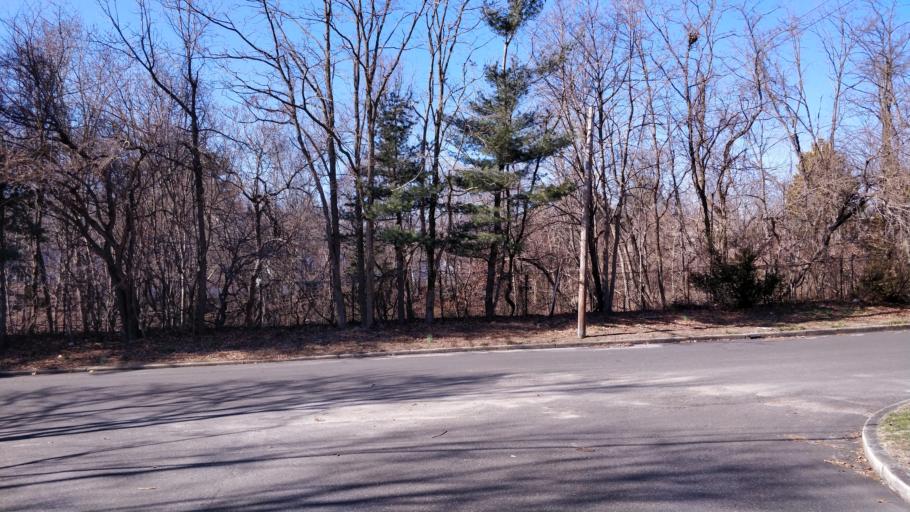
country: US
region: New York
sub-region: Suffolk County
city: Setauket-East Setauket
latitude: 40.9285
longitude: -73.1112
